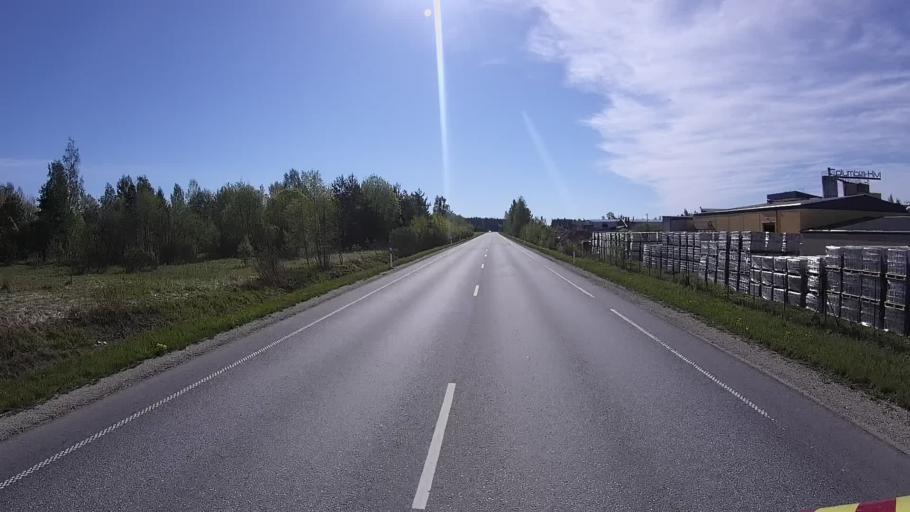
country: EE
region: Tartu
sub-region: Tartu linn
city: Tartu
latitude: 58.3526
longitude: 26.9200
